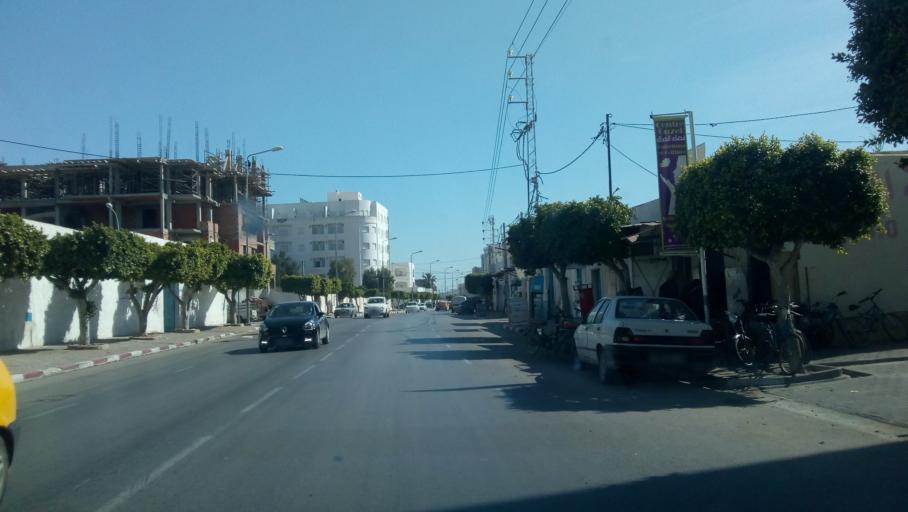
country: TN
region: Safaqis
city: Sfax
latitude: 34.7840
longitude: 10.7219
